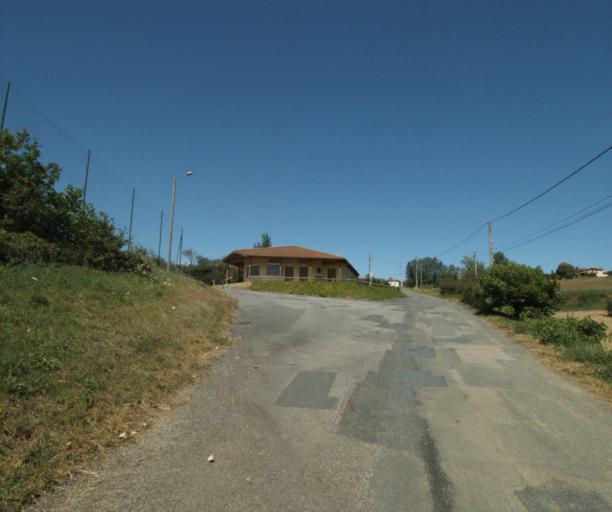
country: FR
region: Rhone-Alpes
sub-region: Departement du Rhone
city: Bessenay
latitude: 45.7911
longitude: 4.5596
